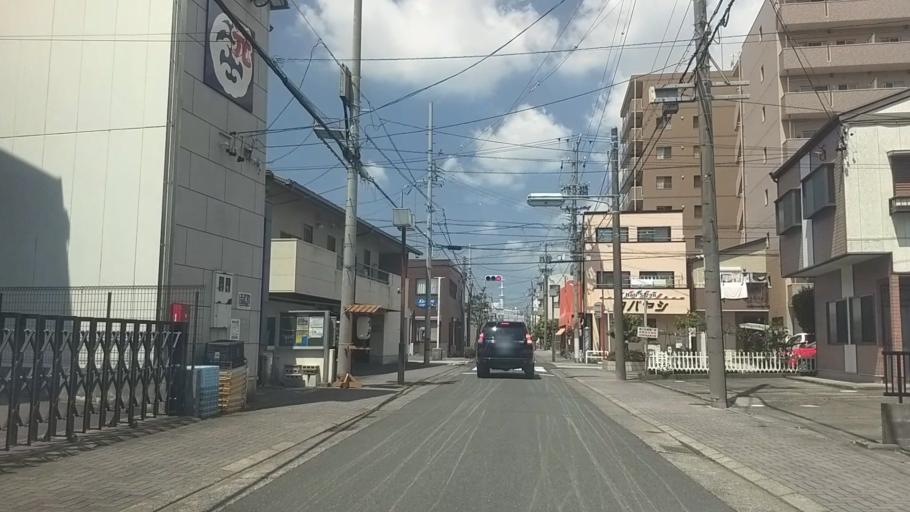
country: JP
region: Shizuoka
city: Hamamatsu
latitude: 34.7148
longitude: 137.7329
